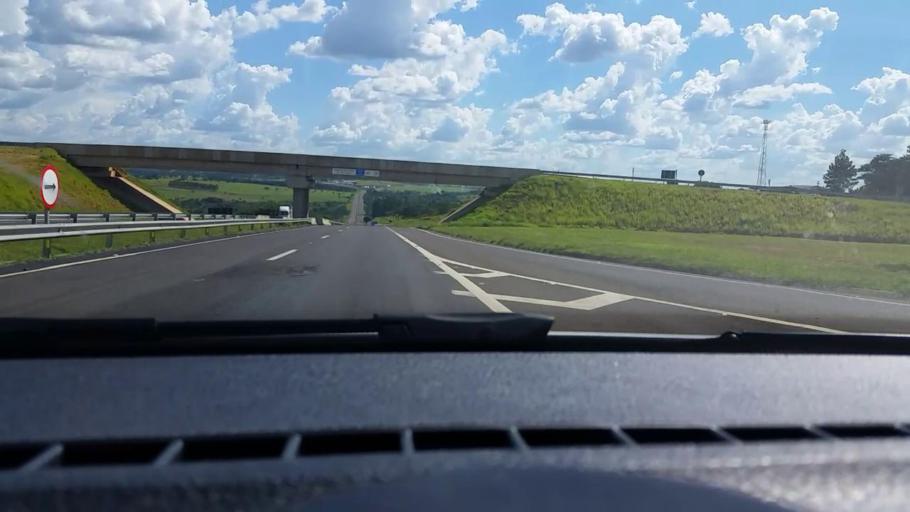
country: BR
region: Sao Paulo
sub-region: Bauru
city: Bauru
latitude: -22.3978
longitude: -49.0873
